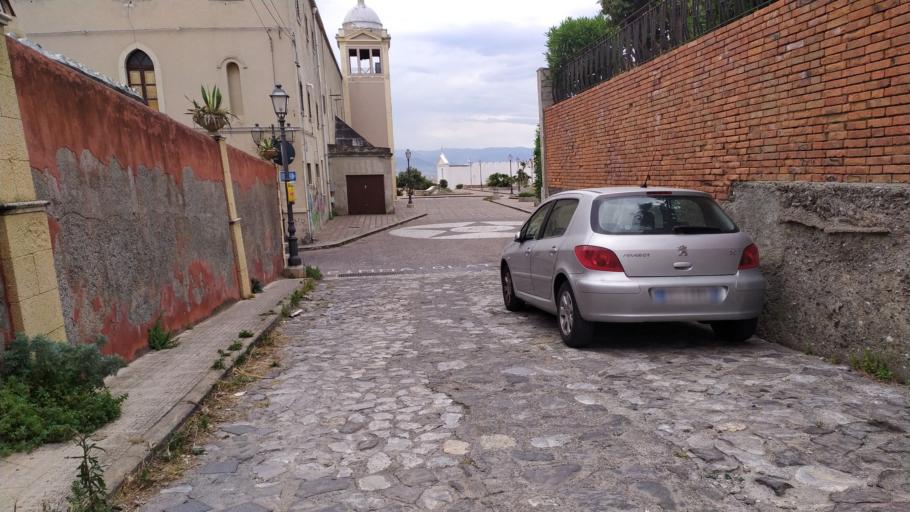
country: IT
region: Sicily
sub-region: Messina
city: Milazzo
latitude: 38.2282
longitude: 15.2418
